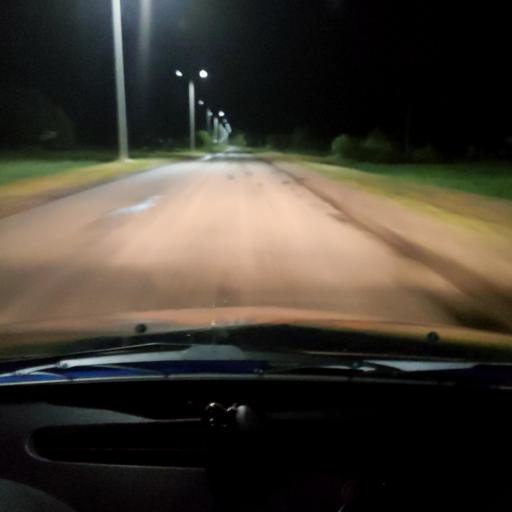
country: RU
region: Voronezj
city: Khrenovoye
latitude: 51.1250
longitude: 40.2775
